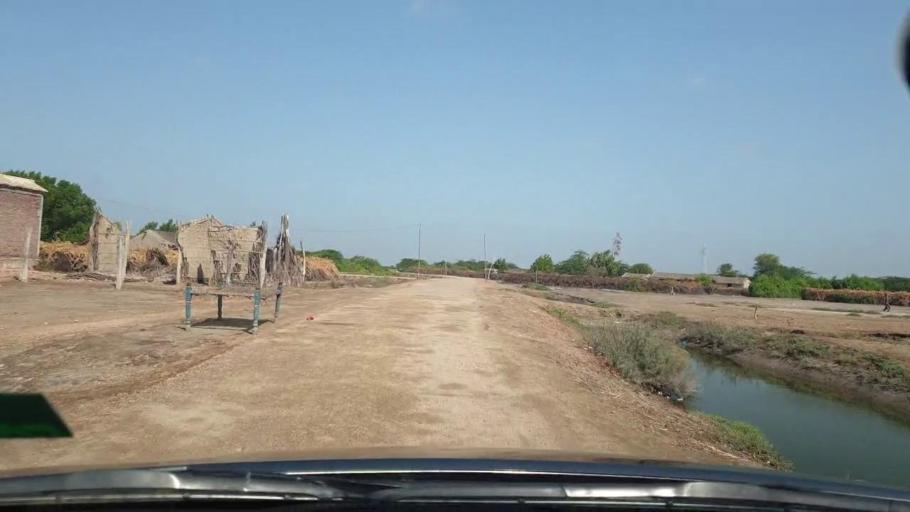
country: PK
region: Sindh
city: Tando Bago
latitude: 24.7466
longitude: 68.9786
